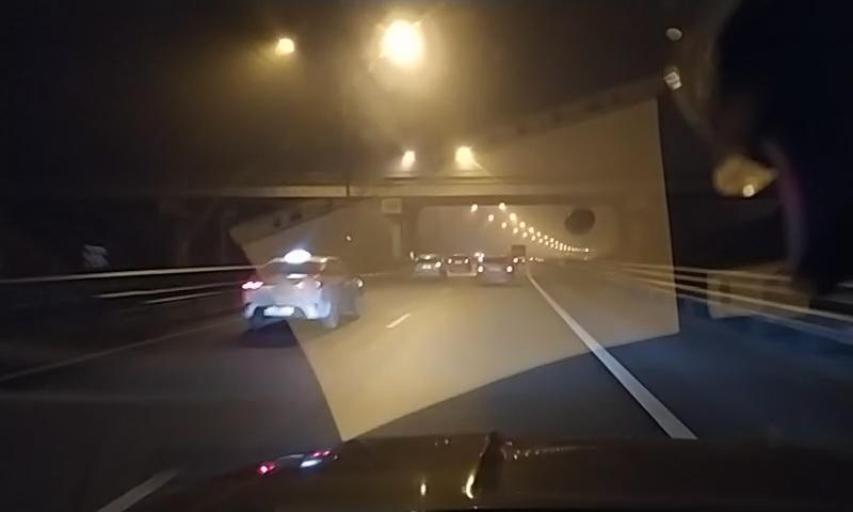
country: RU
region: Leningrad
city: Bugry
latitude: 60.1200
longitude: 30.3854
